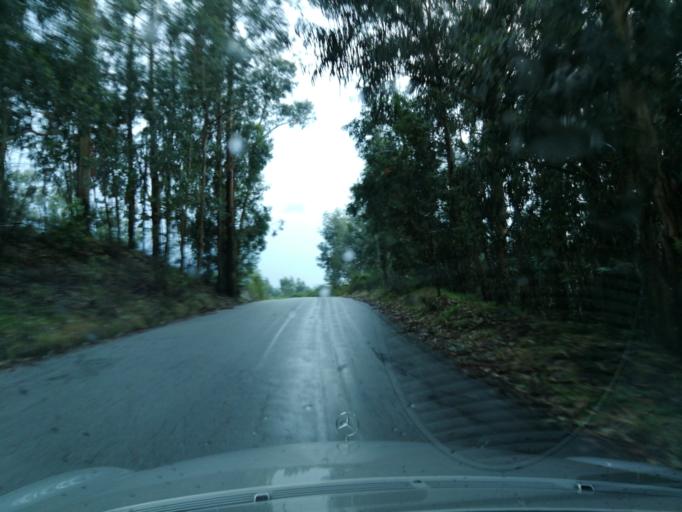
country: PT
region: Braga
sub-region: Vila Nova de Famalicao
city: Joane
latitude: 41.4622
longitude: -8.4352
